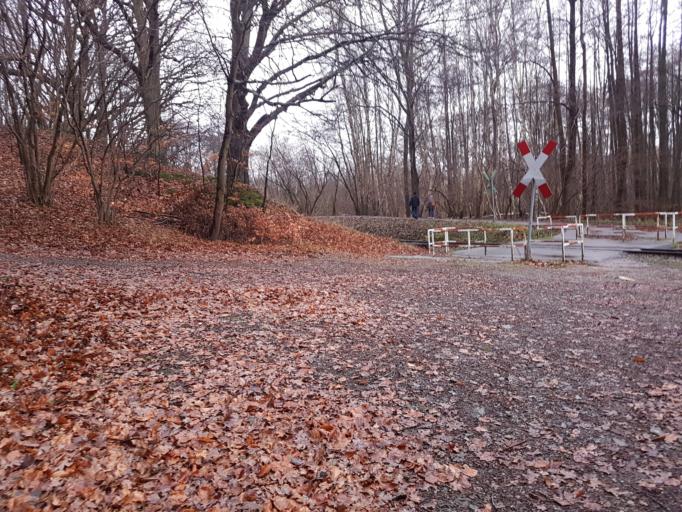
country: DE
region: Mecklenburg-Vorpommern
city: Ostseebad Binz
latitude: 54.3903
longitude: 13.5965
